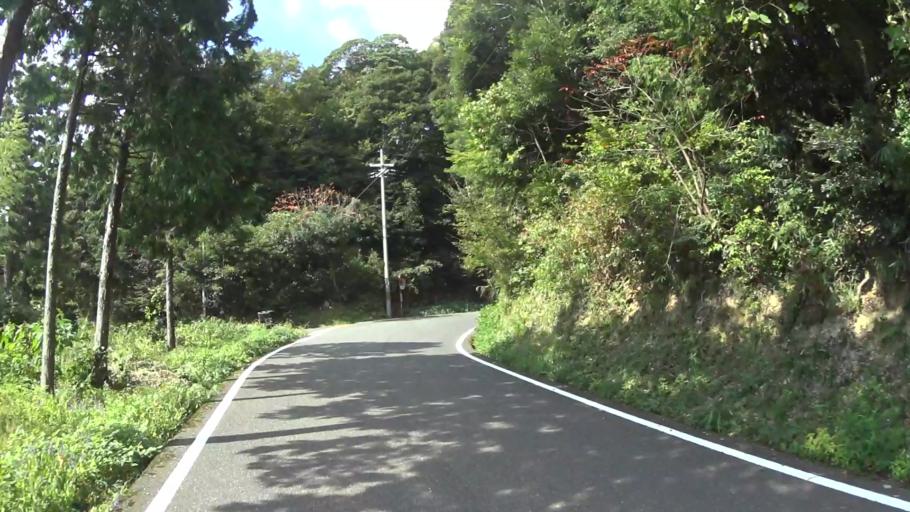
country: JP
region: Kyoto
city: Miyazu
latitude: 35.6805
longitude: 135.2675
